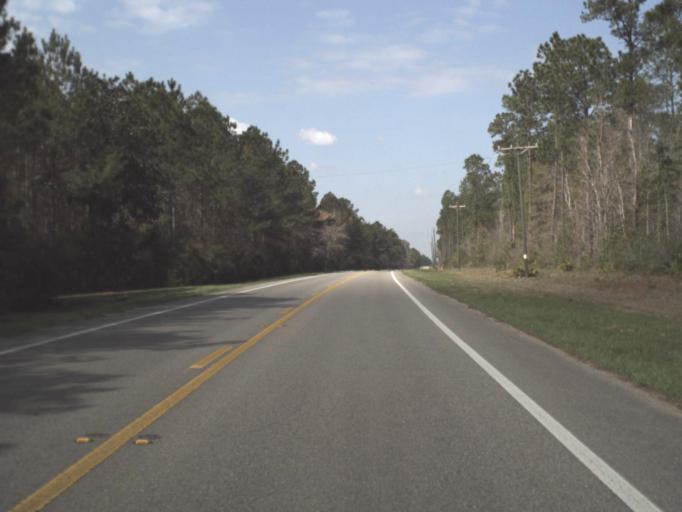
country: US
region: Florida
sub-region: Liberty County
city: Bristol
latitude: 30.3834
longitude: -84.7371
